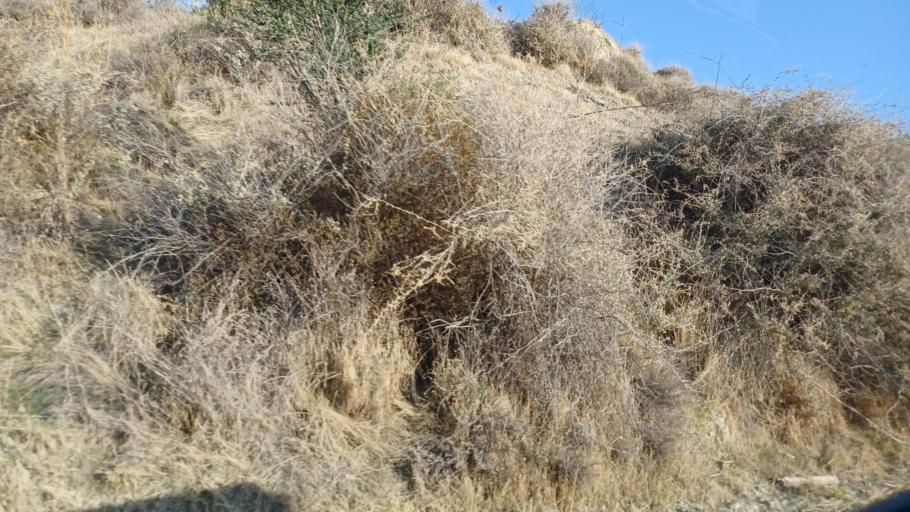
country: CY
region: Pafos
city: Polis
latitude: 34.9970
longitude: 32.4587
